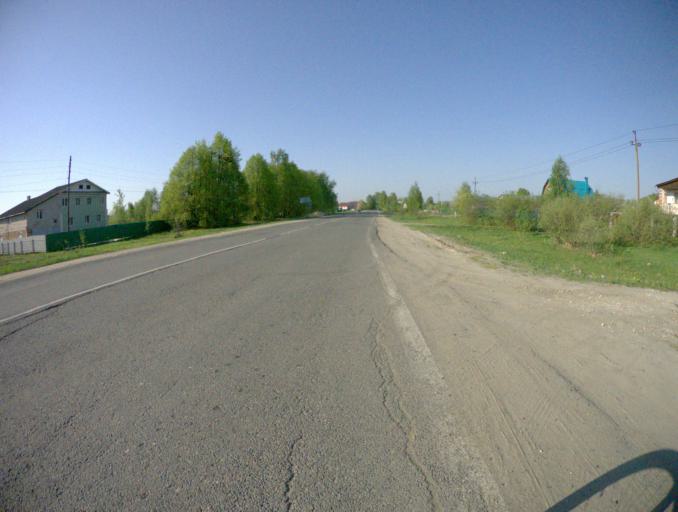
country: RU
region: Vladimir
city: Novovyazniki
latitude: 56.2181
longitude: 42.1830
